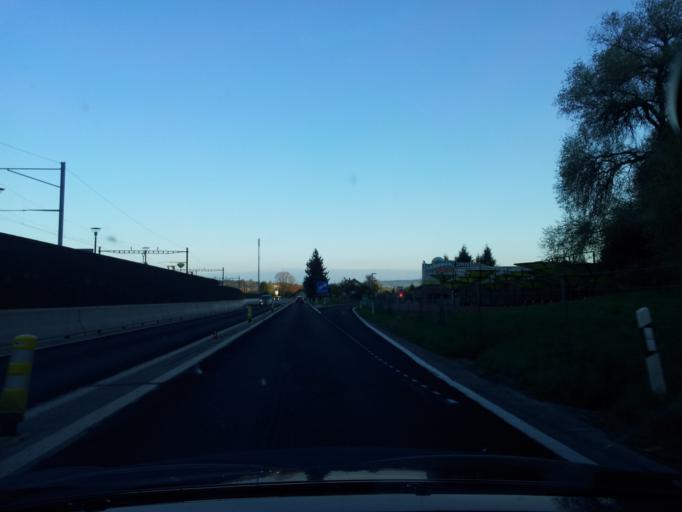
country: CH
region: Bern
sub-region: Seeland District
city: Worben
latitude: 47.1125
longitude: 7.2998
